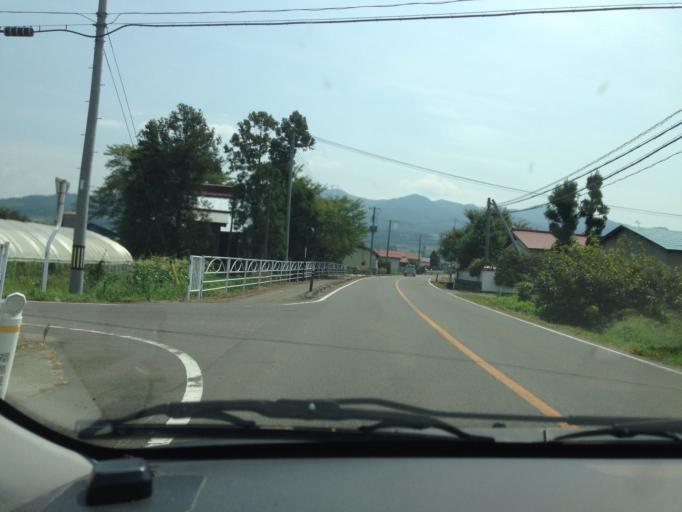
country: JP
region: Fukushima
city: Kitakata
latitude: 37.6451
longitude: 139.9101
